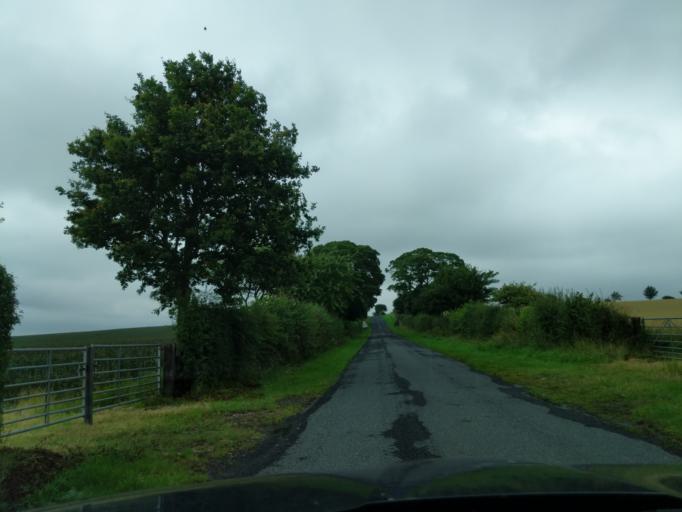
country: GB
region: England
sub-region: Northumberland
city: Ford
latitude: 55.6983
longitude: -2.1423
